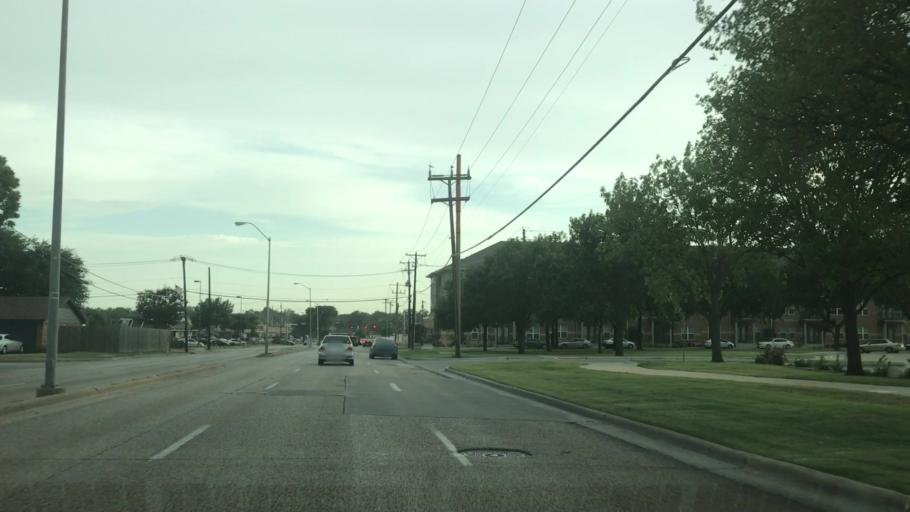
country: US
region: Texas
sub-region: Dallas County
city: Mesquite
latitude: 32.8253
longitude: -96.6443
